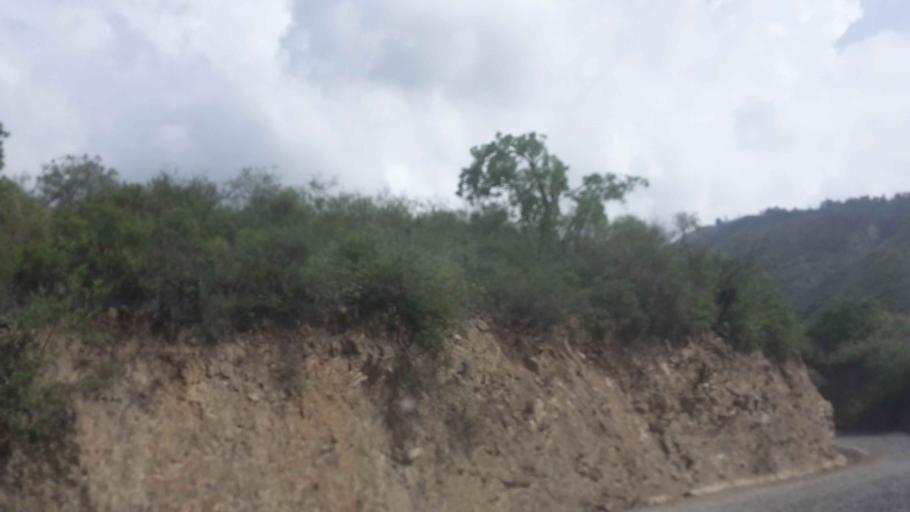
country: BO
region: Cochabamba
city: Cochabamba
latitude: -17.3722
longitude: -66.0618
